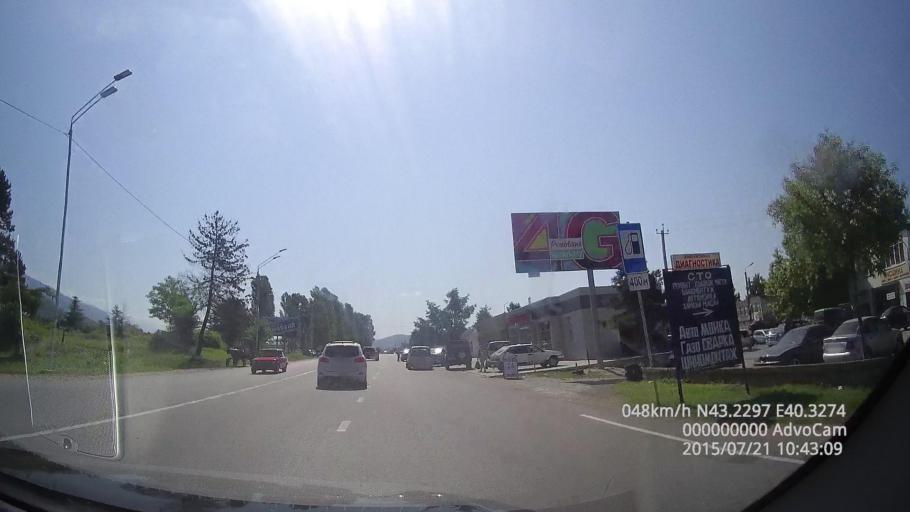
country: GE
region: Abkhazia
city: Bich'vinta
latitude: 43.2297
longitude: 40.3276
